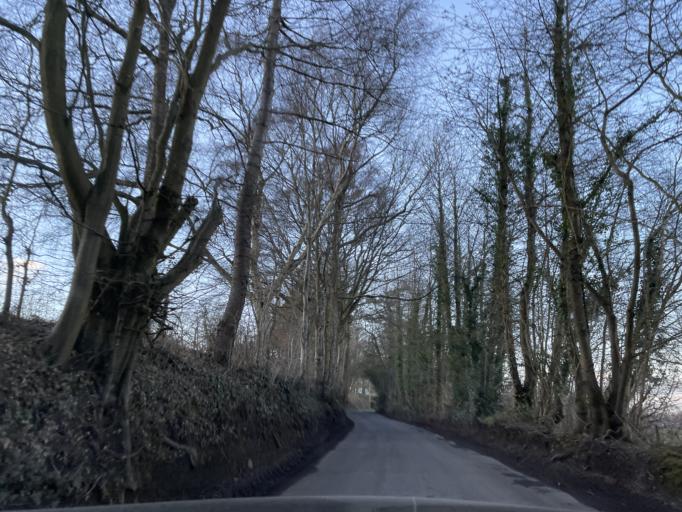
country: GB
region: England
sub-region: Kent
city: Westerham
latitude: 51.2590
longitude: 0.1224
